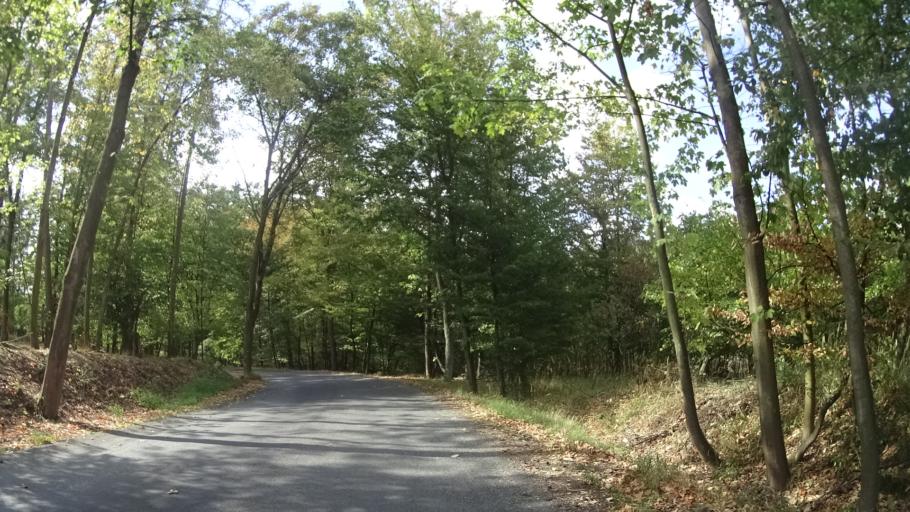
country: CZ
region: Olomoucky
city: Bila Lhota
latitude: 49.7328
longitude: 17.0071
